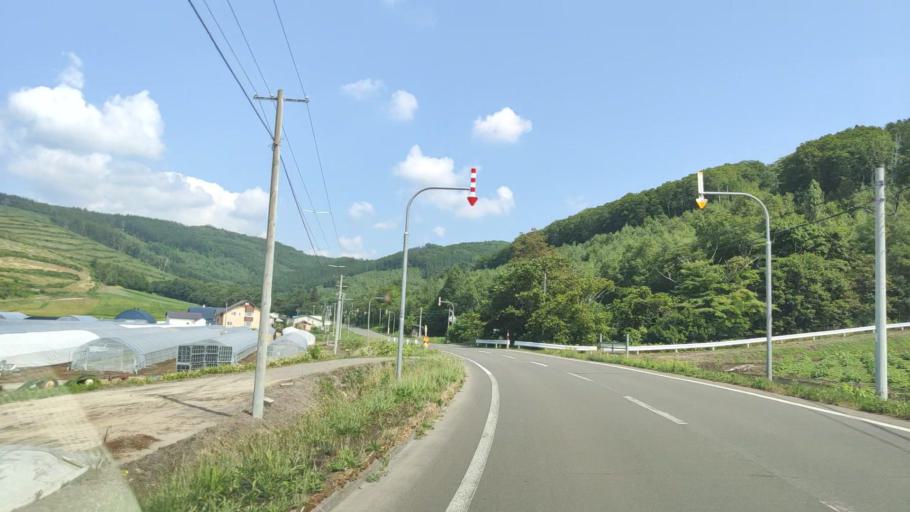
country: JP
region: Hokkaido
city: Shimo-furano
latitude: 43.4195
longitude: 142.4021
